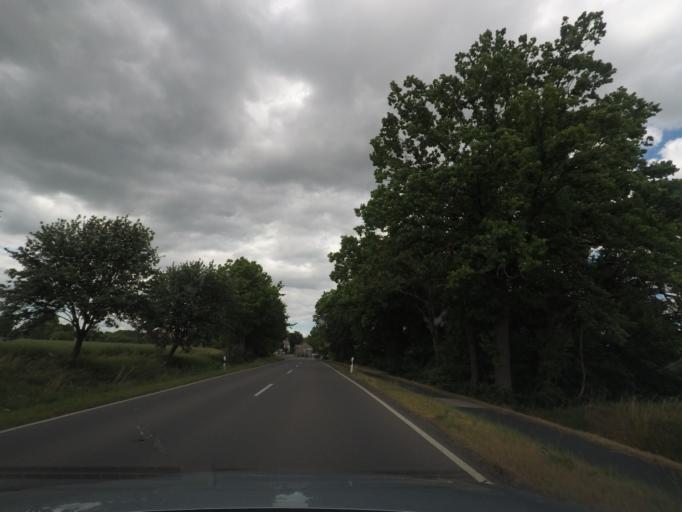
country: DE
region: Saxony-Anhalt
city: Ausleben
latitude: 52.0251
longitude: 11.0937
